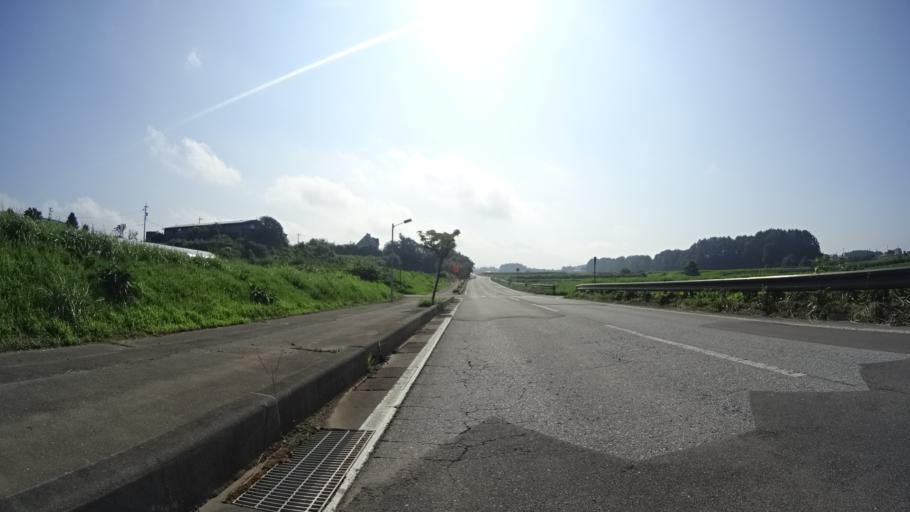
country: JP
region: Nagano
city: Chino
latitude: 35.9659
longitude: 138.2000
